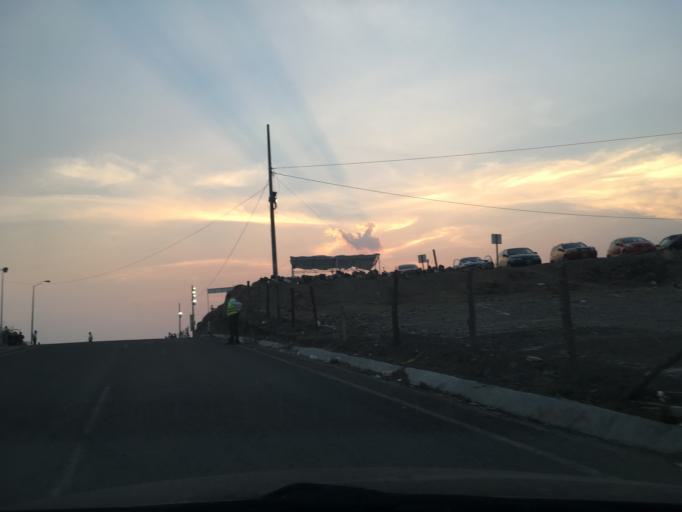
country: MX
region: Michoacan
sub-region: Morelia
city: La Aldea
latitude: 19.7299
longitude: -101.0902
